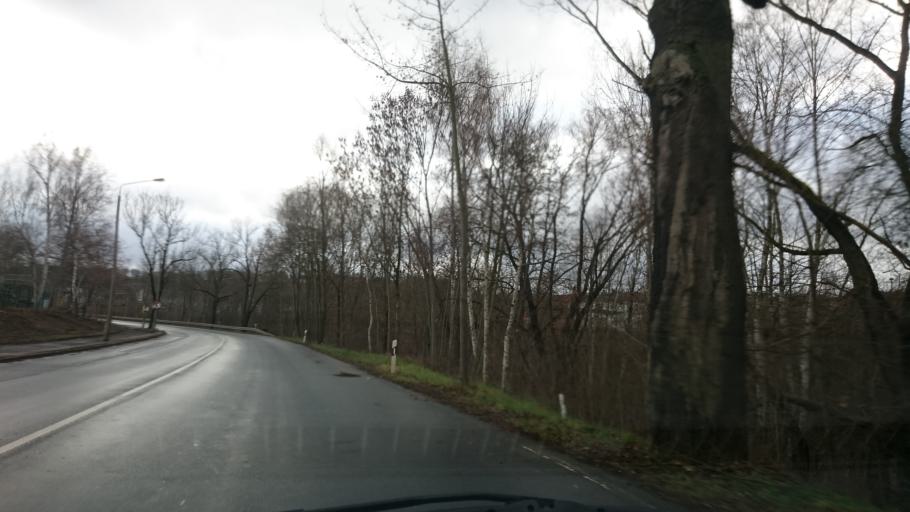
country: DE
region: Saxony
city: Wilkau-Hasslau
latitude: 50.6890
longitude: 12.4960
